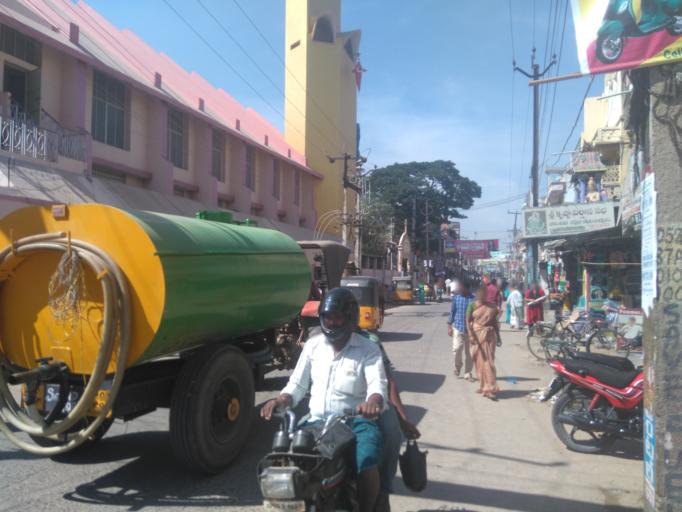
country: IN
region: Andhra Pradesh
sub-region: Chittoor
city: Chittoor
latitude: 13.2175
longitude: 79.0973
